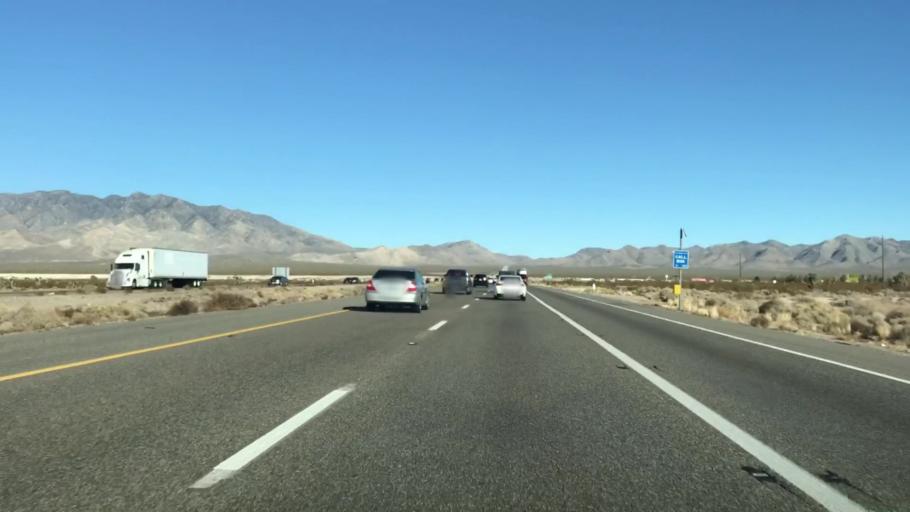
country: US
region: Nevada
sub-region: Clark County
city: Sandy Valley
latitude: 35.4383
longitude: -115.6894
